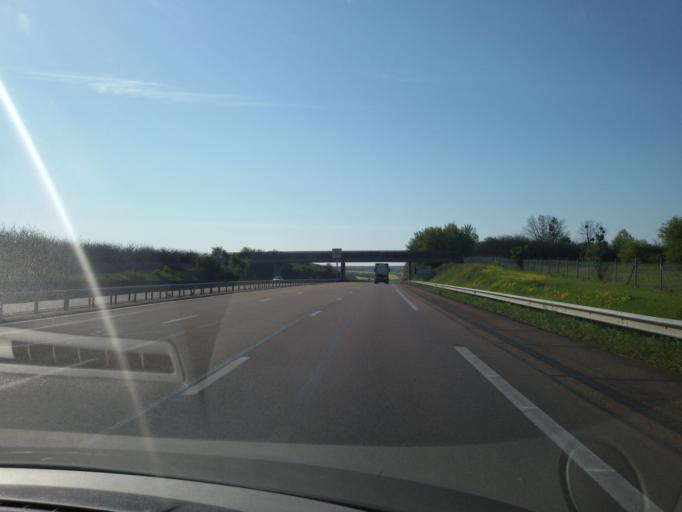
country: FR
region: Bourgogne
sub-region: Departement de l'Yonne
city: Saint-Julien-du-Sault
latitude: 47.9590
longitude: 3.2202
